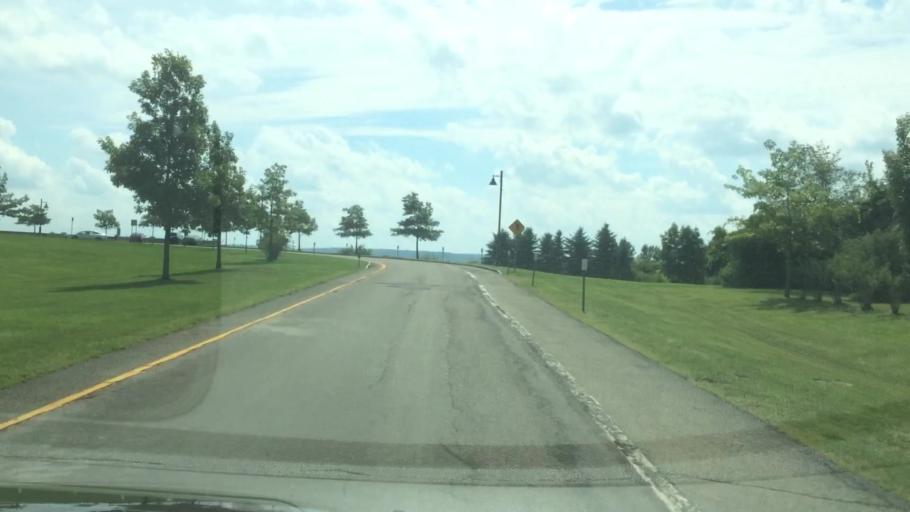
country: US
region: New York
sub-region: Chautauqua County
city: Lakewood
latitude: 42.1353
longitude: -79.3501
